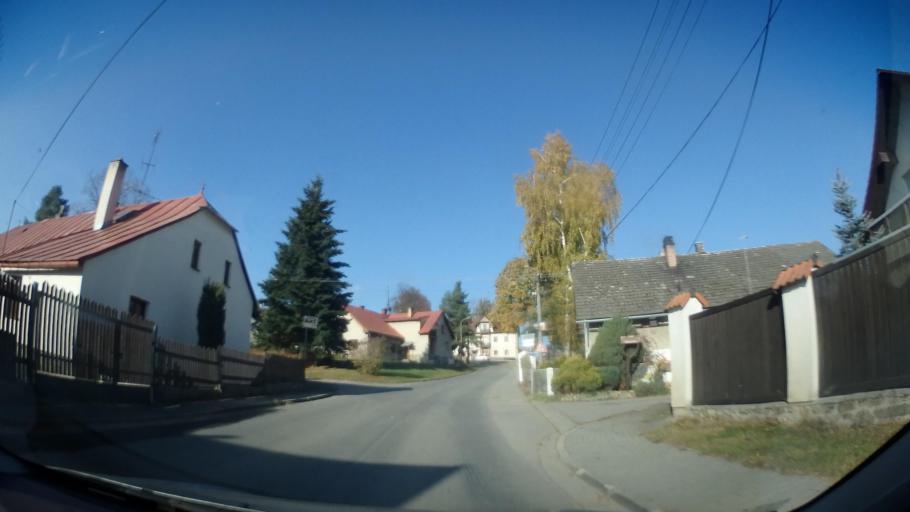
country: CZ
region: Vysocina
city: Zd'ar nad Sazavou Druhy
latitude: 49.6069
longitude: 15.9173
